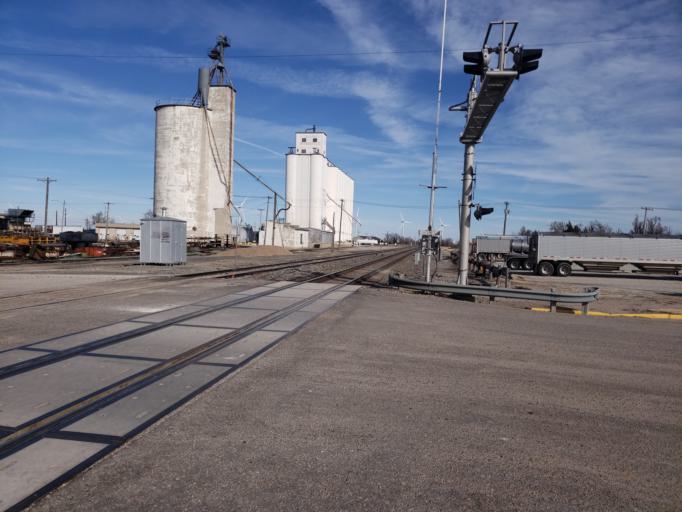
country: US
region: Kansas
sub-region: Hodgeman County
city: Jetmore
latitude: 37.8510
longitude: -99.7576
